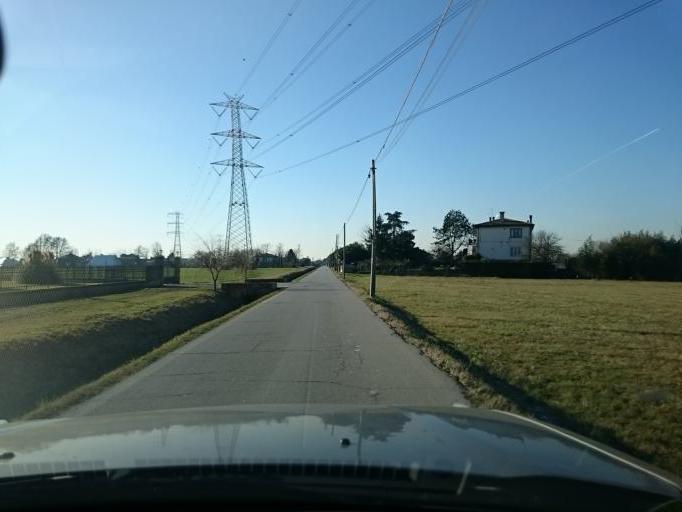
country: IT
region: Veneto
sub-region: Provincia di Venezia
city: Fornase
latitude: 45.4337
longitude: 12.1629
